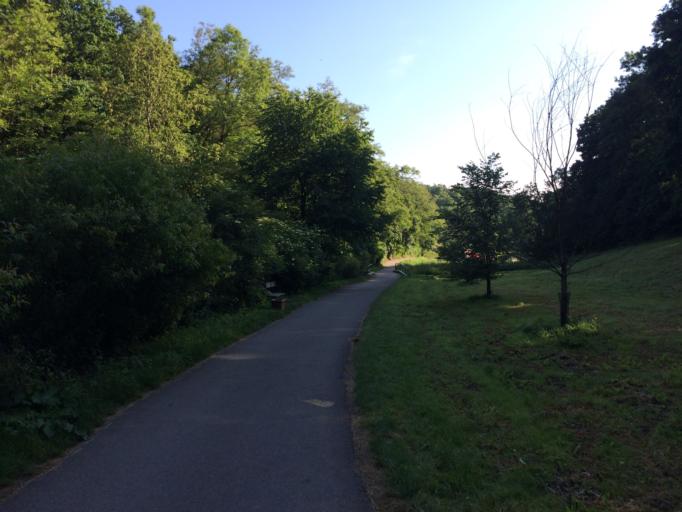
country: CZ
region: Central Bohemia
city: Horomerice
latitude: 50.0966
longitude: 14.3164
